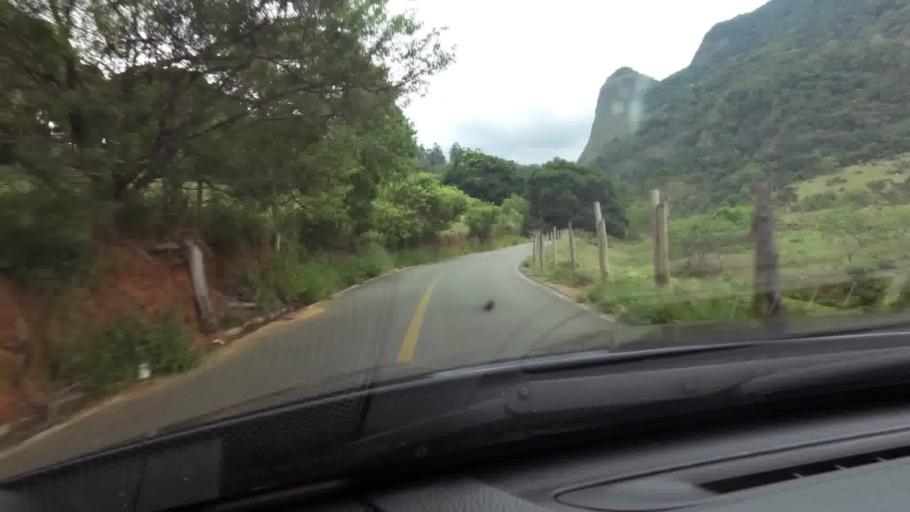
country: BR
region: Espirito Santo
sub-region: Guarapari
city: Guarapari
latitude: -20.6182
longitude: -40.5297
